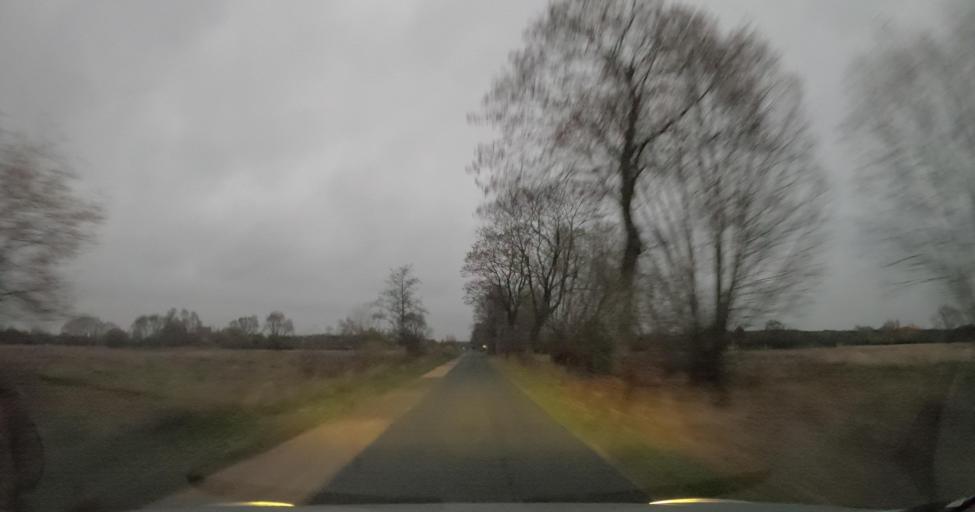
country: PL
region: West Pomeranian Voivodeship
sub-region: Powiat bialogardzki
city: Tychowo
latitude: 53.8673
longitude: 16.2313
